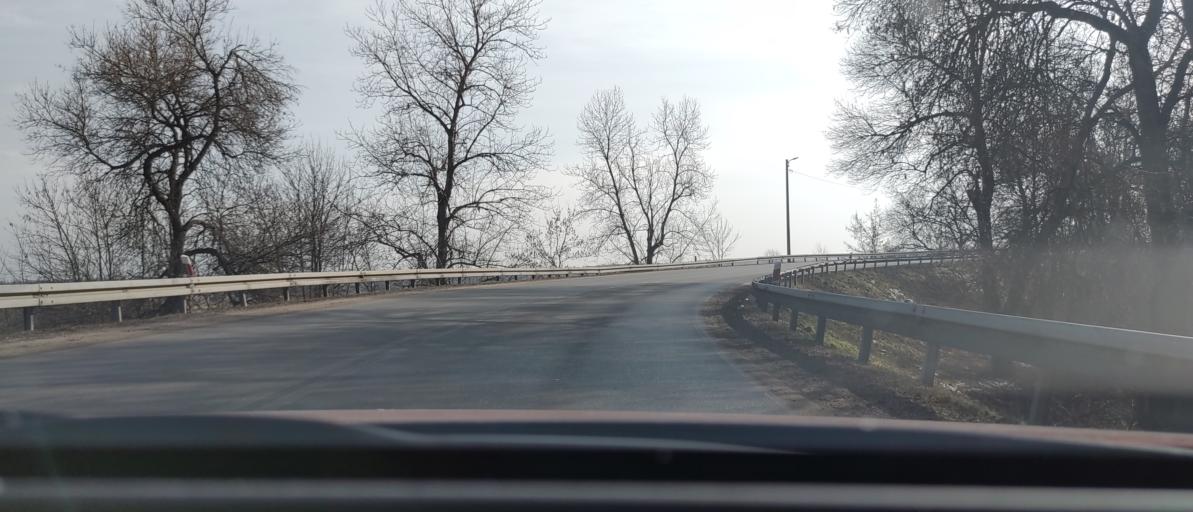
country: PL
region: Masovian Voivodeship
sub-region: Powiat bialobrzeski
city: Bialobrzegi
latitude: 51.6603
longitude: 20.9528
